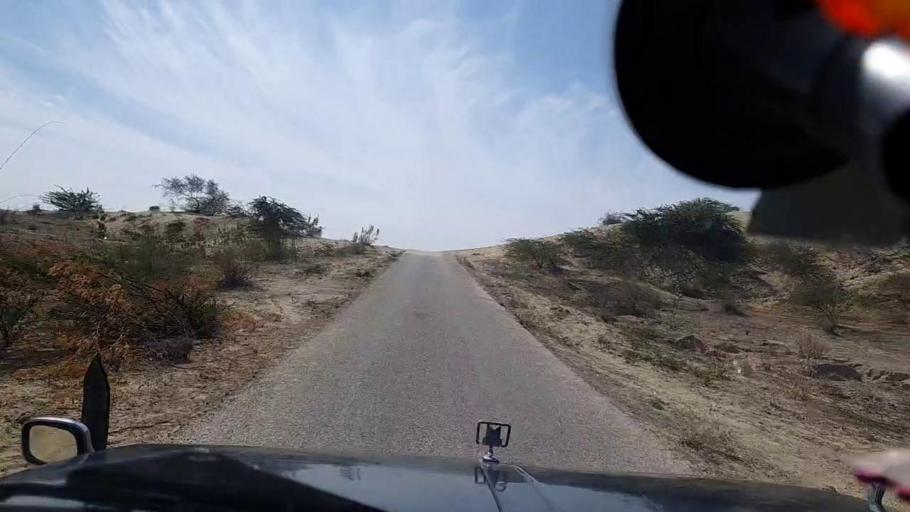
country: PK
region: Sindh
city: Diplo
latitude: 24.3991
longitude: 69.5888
